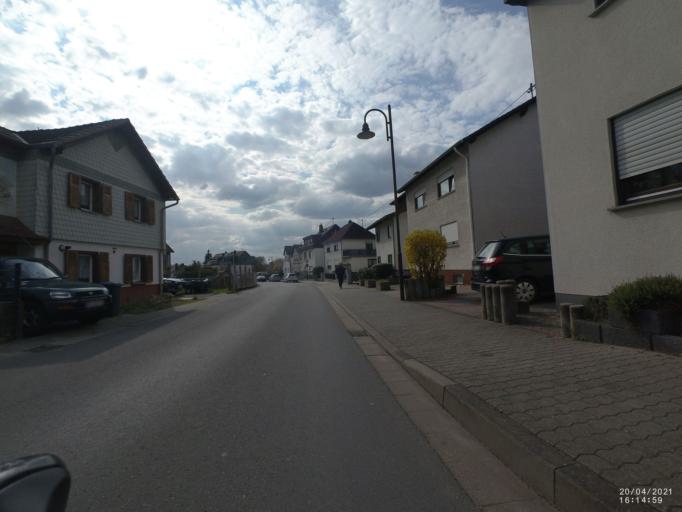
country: DE
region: Rheinland-Pfalz
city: Bendorf
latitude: 50.4270
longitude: 7.5810
